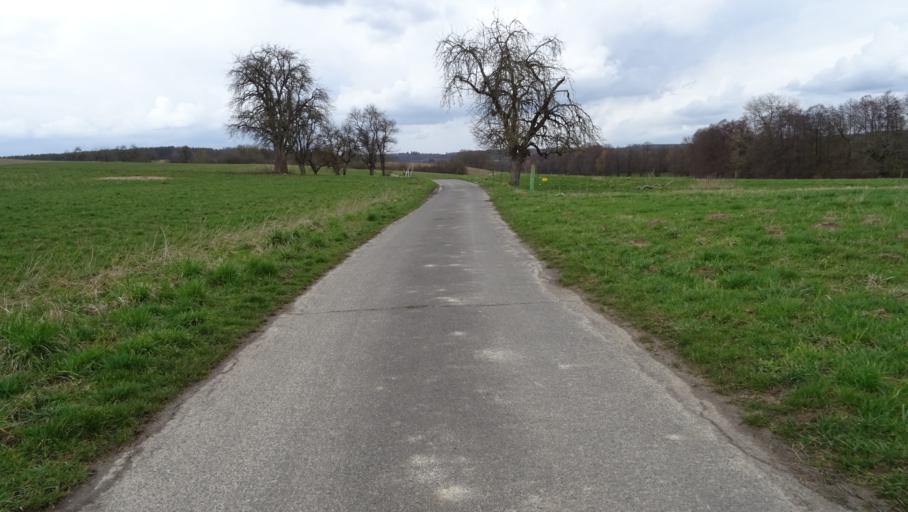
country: DE
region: Baden-Wuerttemberg
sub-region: Karlsruhe Region
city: Seckach
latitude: 49.4284
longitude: 9.2856
